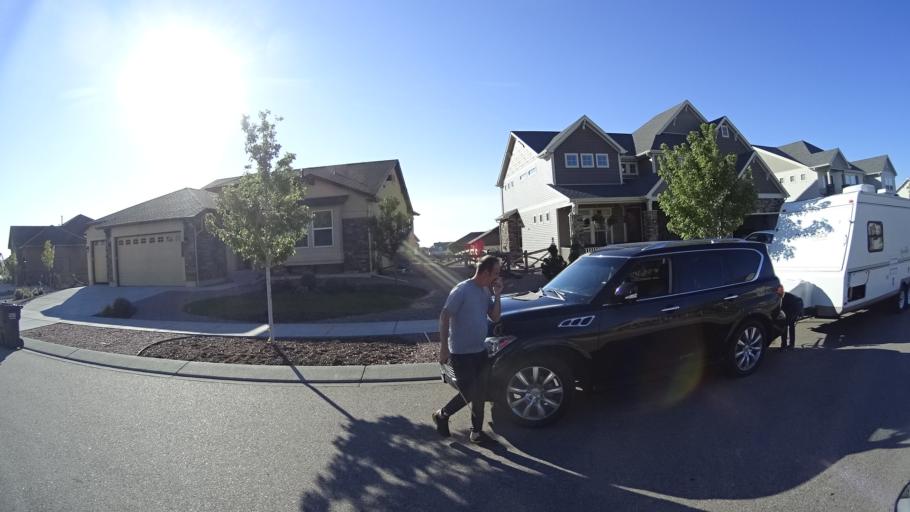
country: US
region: Colorado
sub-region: El Paso County
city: Cimarron Hills
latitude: 38.9358
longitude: -104.6694
